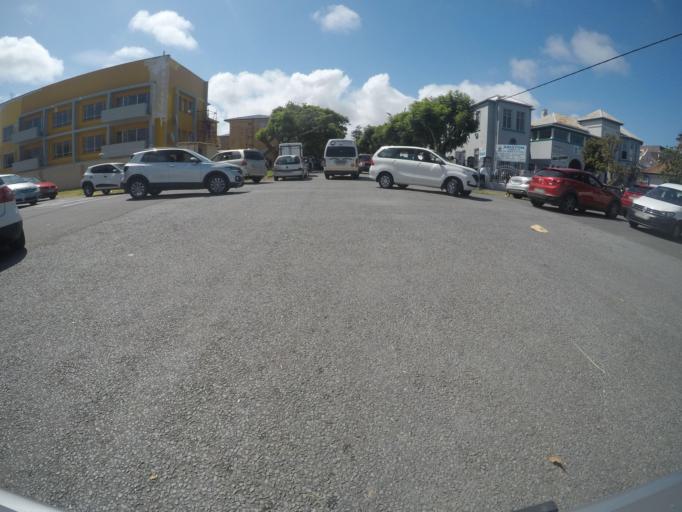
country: ZA
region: Eastern Cape
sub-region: Buffalo City Metropolitan Municipality
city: East London
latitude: -33.0032
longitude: 27.8980
